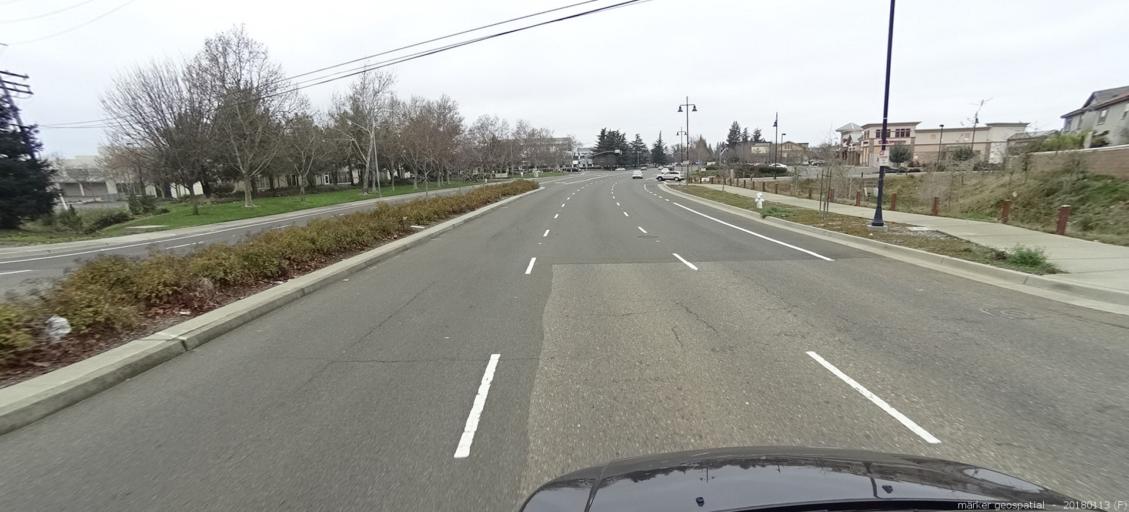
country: US
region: California
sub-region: Sacramento County
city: Rancho Cordova
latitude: 38.5803
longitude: -121.2831
